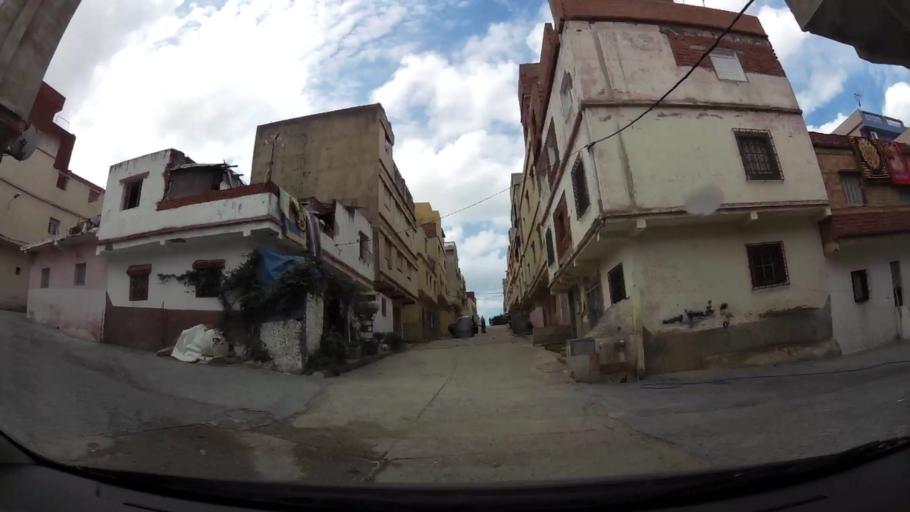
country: MA
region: Tanger-Tetouan
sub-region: Tanger-Assilah
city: Tangier
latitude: 35.7807
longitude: -5.7545
